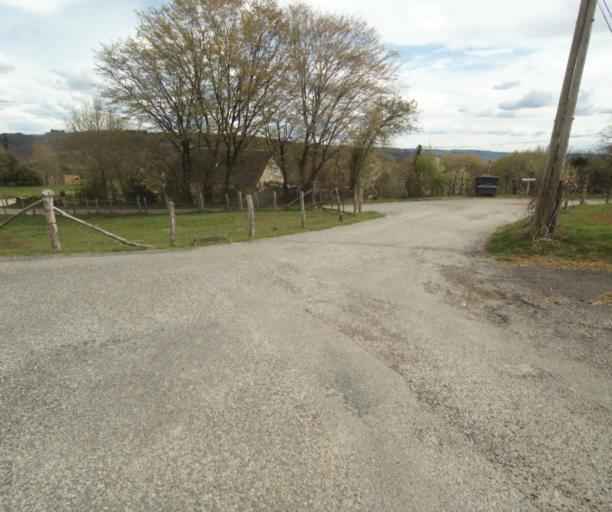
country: FR
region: Limousin
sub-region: Departement de la Correze
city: Argentat
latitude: 45.1792
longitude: 1.9456
